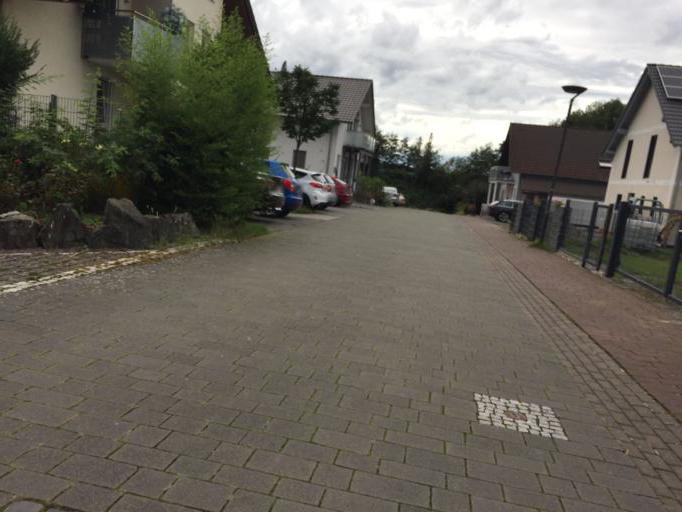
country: DE
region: Hesse
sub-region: Regierungsbezirk Giessen
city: Langgons
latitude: 50.4893
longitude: 8.6686
